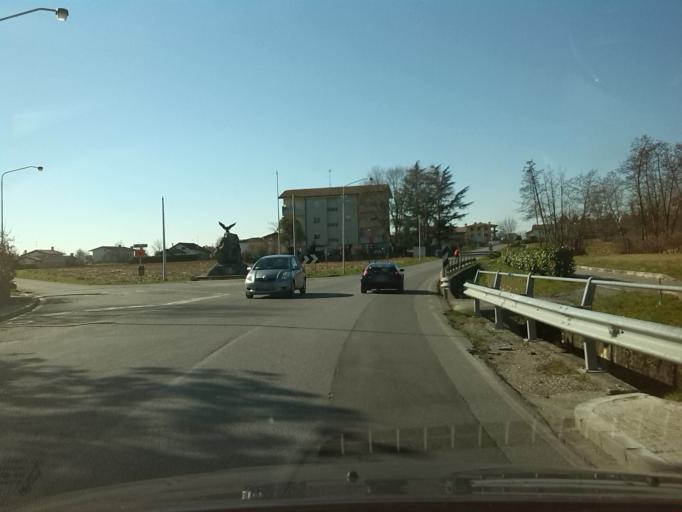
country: IT
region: Friuli Venezia Giulia
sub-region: Provincia di Udine
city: Faedis
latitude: 46.1288
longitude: 13.3592
